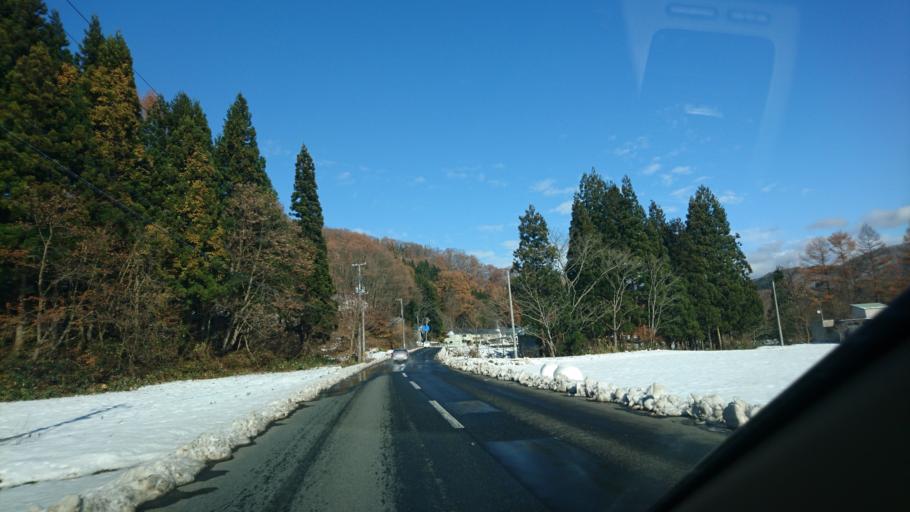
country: JP
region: Akita
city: Yokotemachi
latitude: 39.3430
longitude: 140.7618
